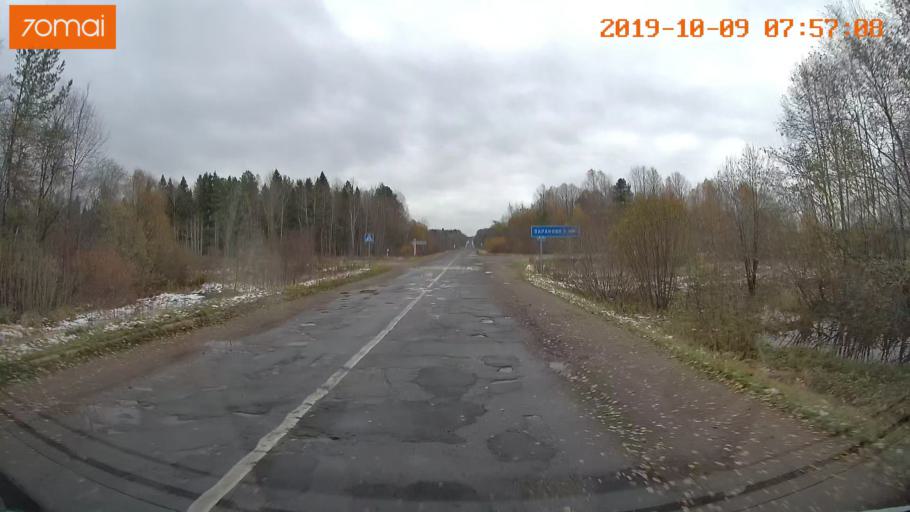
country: RU
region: Jaroslavl
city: Kukoboy
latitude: 58.6970
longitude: 39.9464
